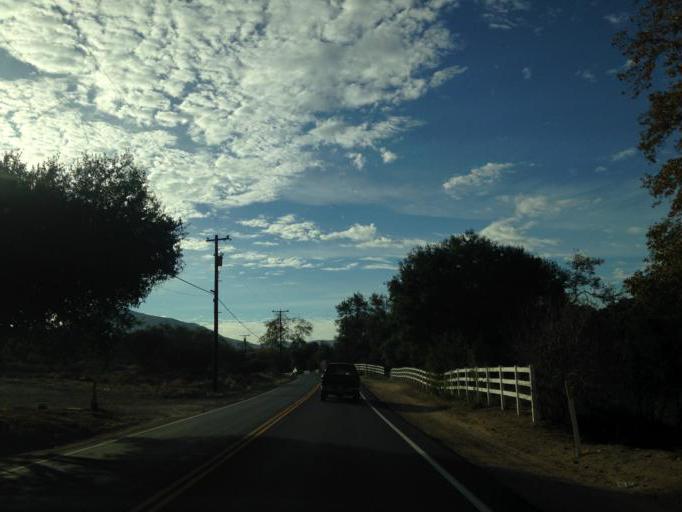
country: US
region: California
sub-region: San Diego County
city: Rainbow
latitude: 33.3796
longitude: -117.0832
